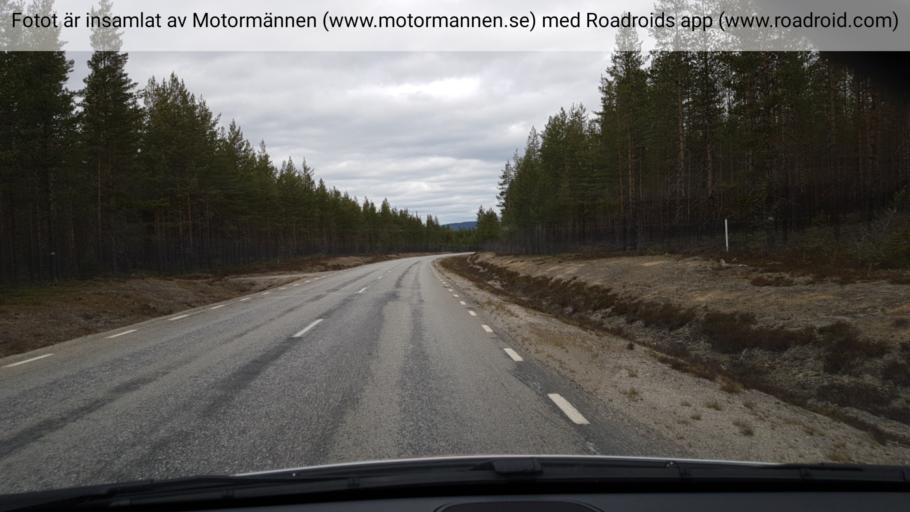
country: SE
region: Vaesterbotten
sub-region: Mala Kommun
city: Mala
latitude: 64.9193
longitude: 18.6292
